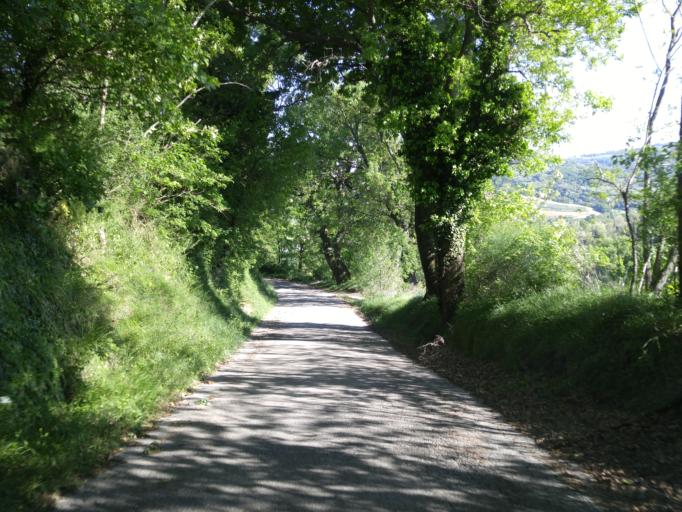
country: IT
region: The Marches
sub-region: Provincia di Pesaro e Urbino
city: Monteciccardo
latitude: 43.8249
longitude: 12.8340
